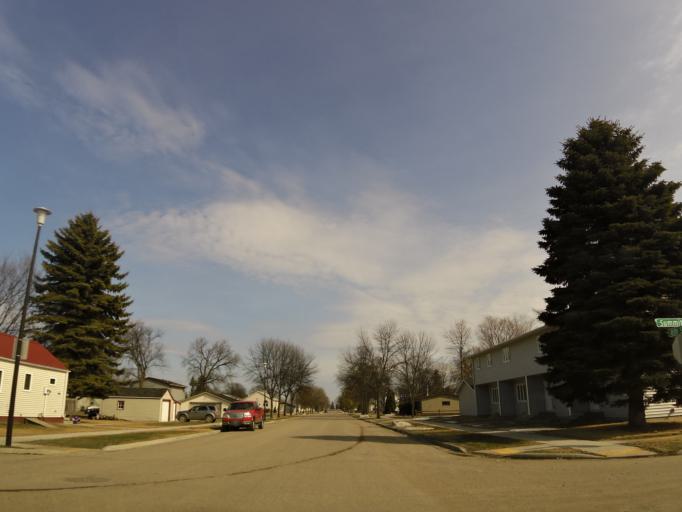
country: US
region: North Dakota
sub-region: Walsh County
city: Grafton
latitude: 48.4165
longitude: -97.4042
